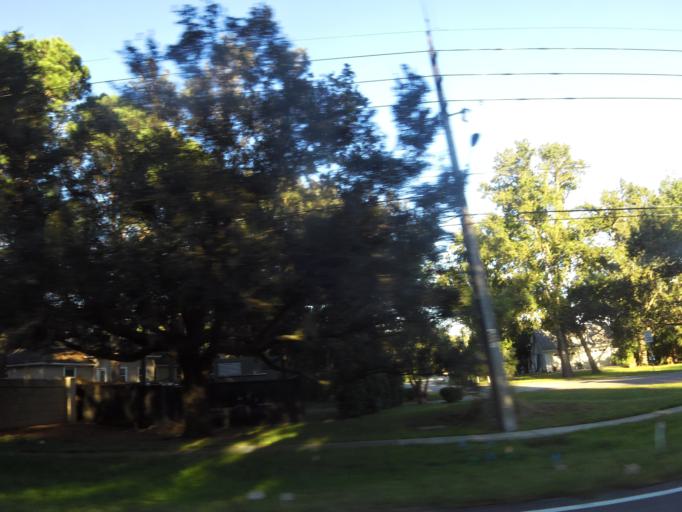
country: US
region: Florida
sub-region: Duval County
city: Neptune Beach
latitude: 30.3076
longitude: -81.4456
